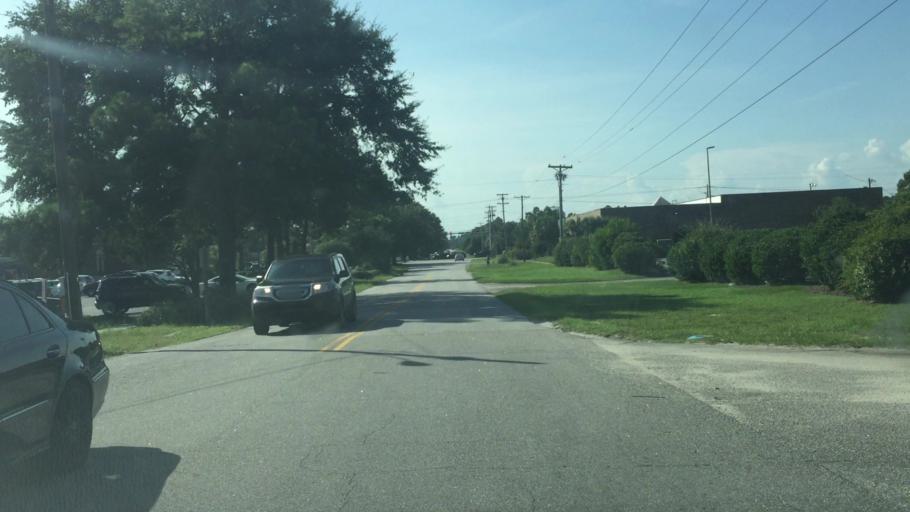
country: US
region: South Carolina
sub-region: Horry County
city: Myrtle Beach
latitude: 33.7478
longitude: -78.8147
